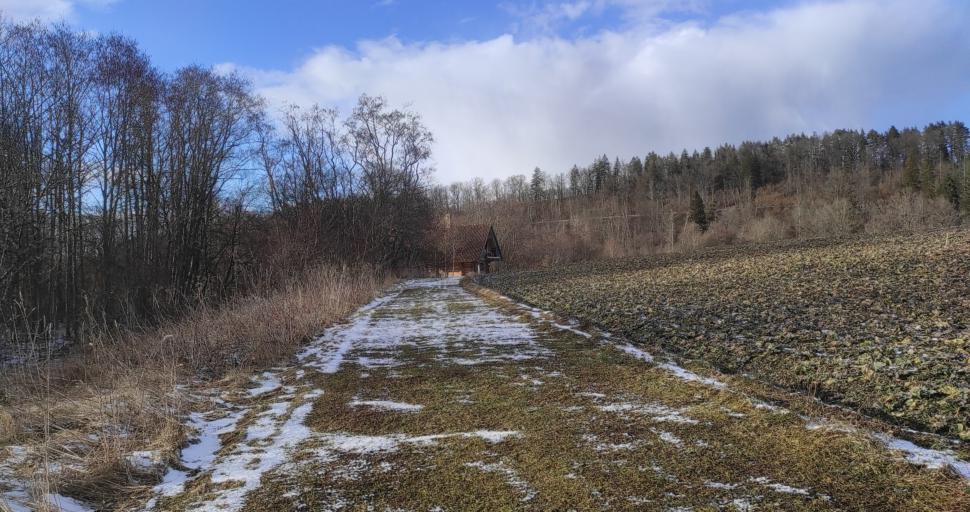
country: LV
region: Talsu Rajons
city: Sabile
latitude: 57.0149
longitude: 22.6239
